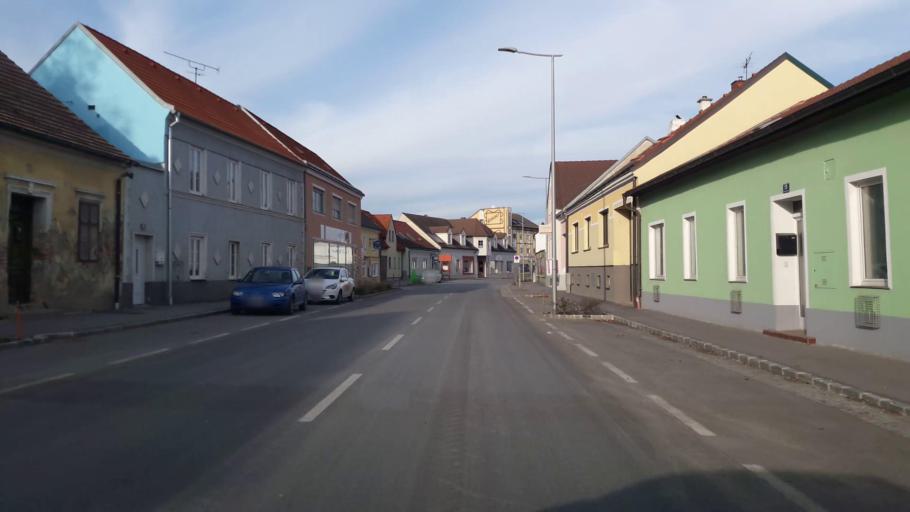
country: AT
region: Lower Austria
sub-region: Politischer Bezirk Mistelbach
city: Gaweinstal
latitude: 48.4745
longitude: 16.5889
